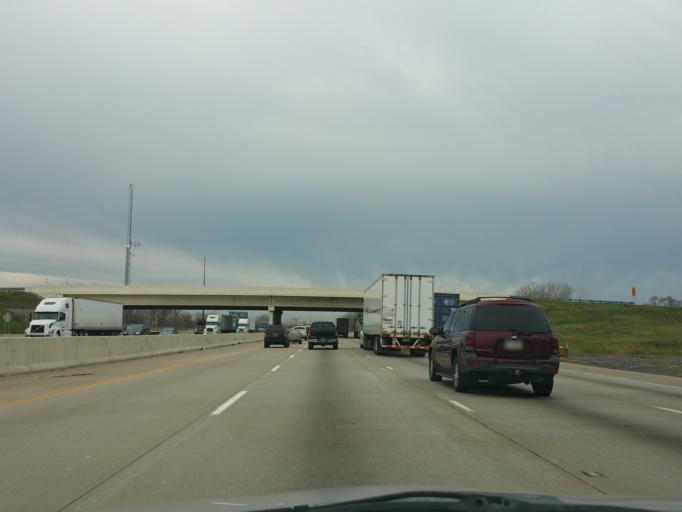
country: US
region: Indiana
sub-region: Lake County
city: Gary
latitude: 41.5675
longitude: -87.3346
